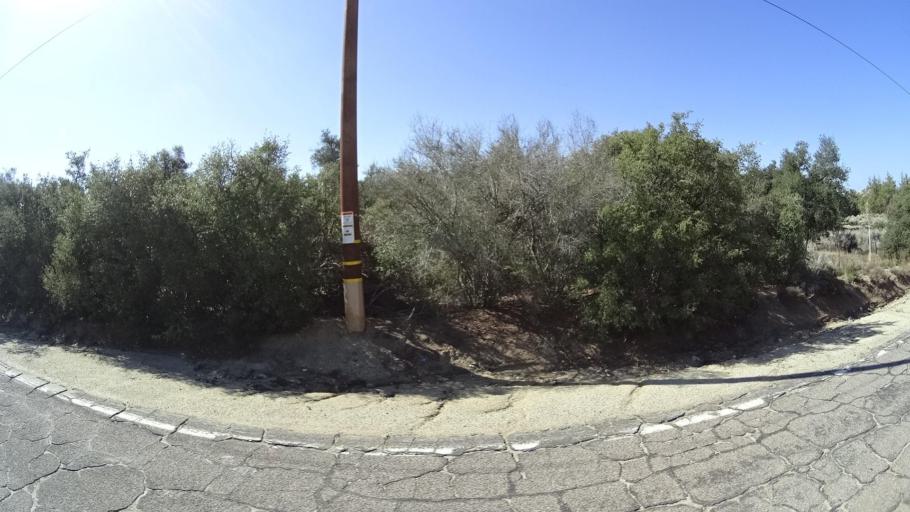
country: US
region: California
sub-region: Riverside County
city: Anza
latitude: 33.3848
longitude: -116.6536
